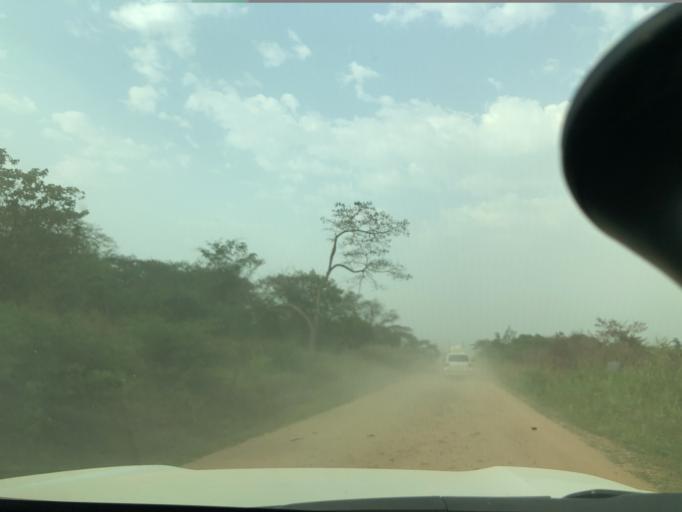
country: UG
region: Western Region
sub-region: Kasese District
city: Margherita
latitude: 0.2109
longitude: 29.6771
